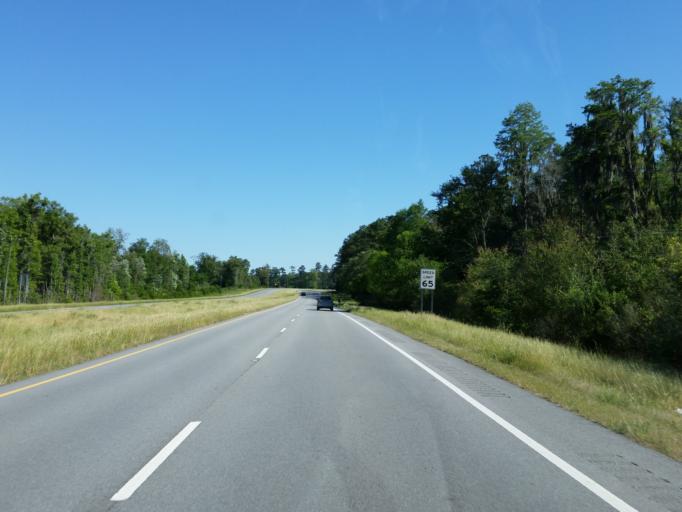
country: US
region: Georgia
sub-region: Lowndes County
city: Valdosta
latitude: 30.7263
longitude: -83.2188
